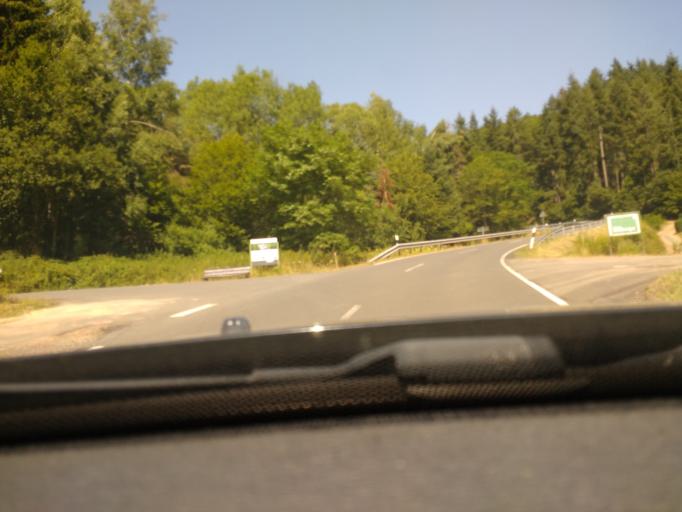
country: DE
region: Rheinland-Pfalz
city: Plein
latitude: 50.0134
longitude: 6.8709
